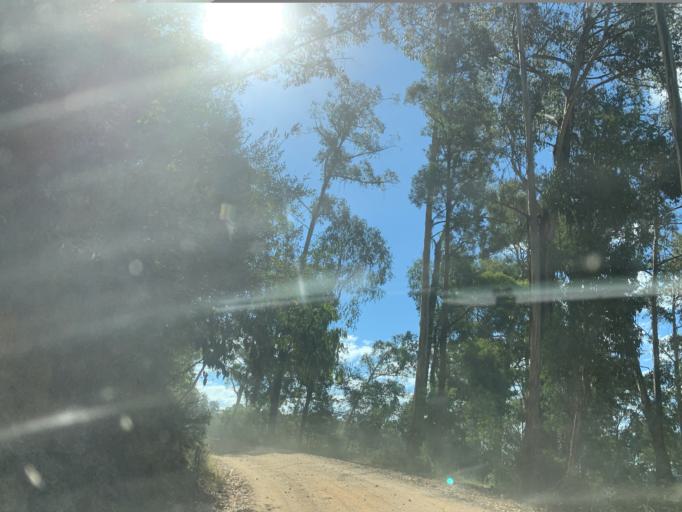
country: AU
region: Victoria
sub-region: Mansfield
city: Mansfield
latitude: -37.0919
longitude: 146.5187
